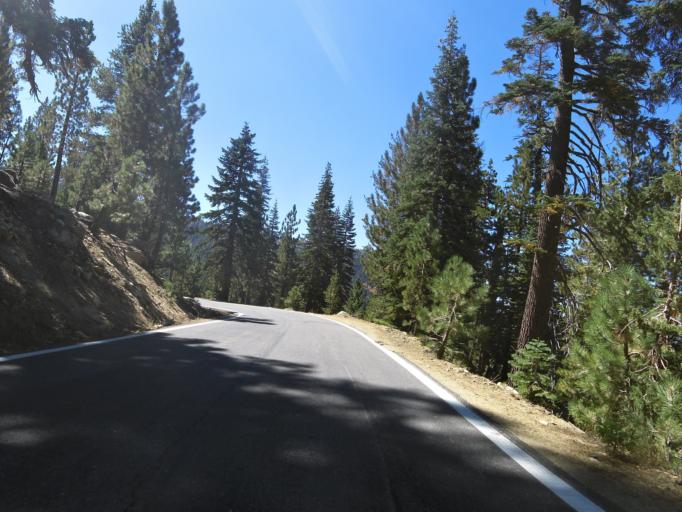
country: US
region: Nevada
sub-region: Douglas County
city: Gardnerville Ranchos
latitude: 38.5511
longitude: -119.8485
